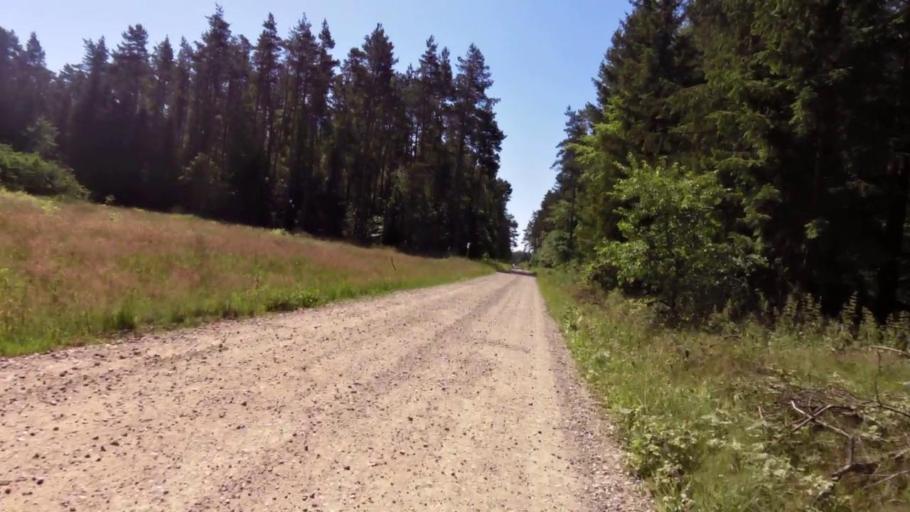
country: PL
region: West Pomeranian Voivodeship
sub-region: Powiat swidwinski
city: Rabino
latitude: 53.9025
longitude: 16.0076
